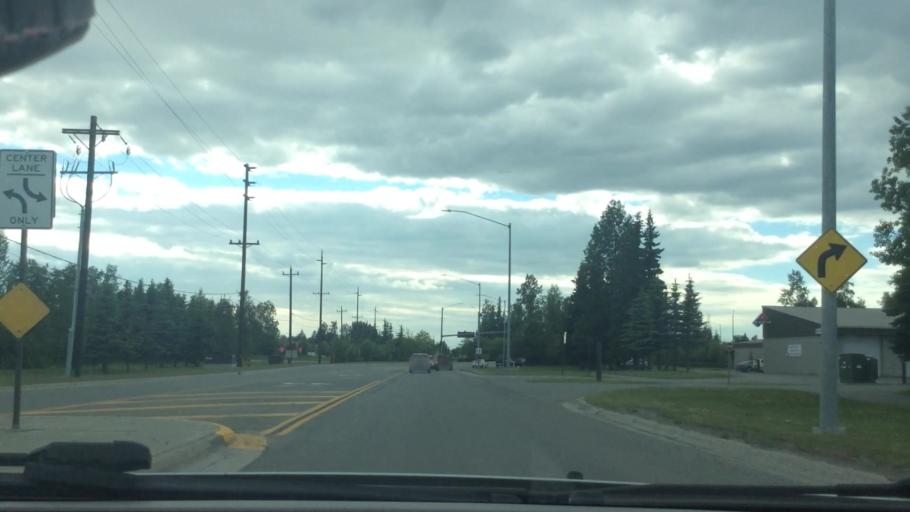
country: US
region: Alaska
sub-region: Anchorage Municipality
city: Elmendorf Air Force Base
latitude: 61.2315
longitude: -149.7639
